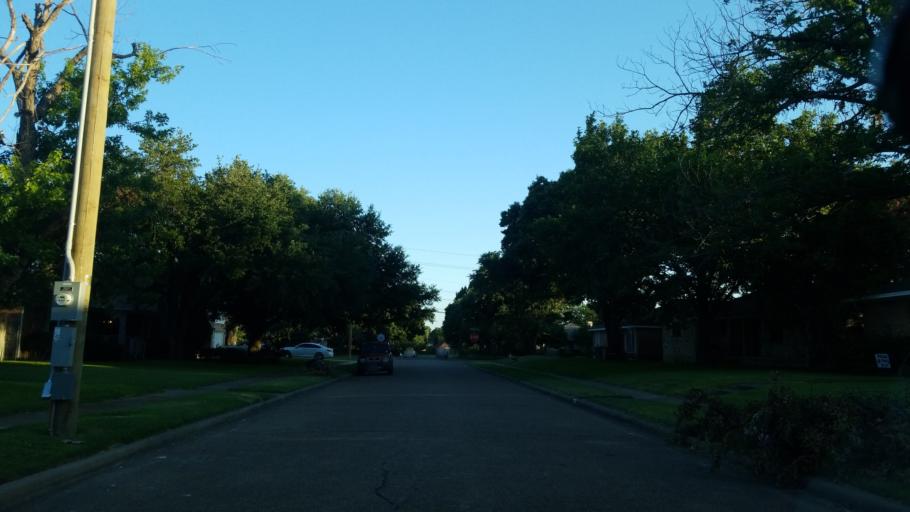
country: US
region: Texas
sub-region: Dallas County
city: Balch Springs
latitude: 32.7893
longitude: -96.6975
